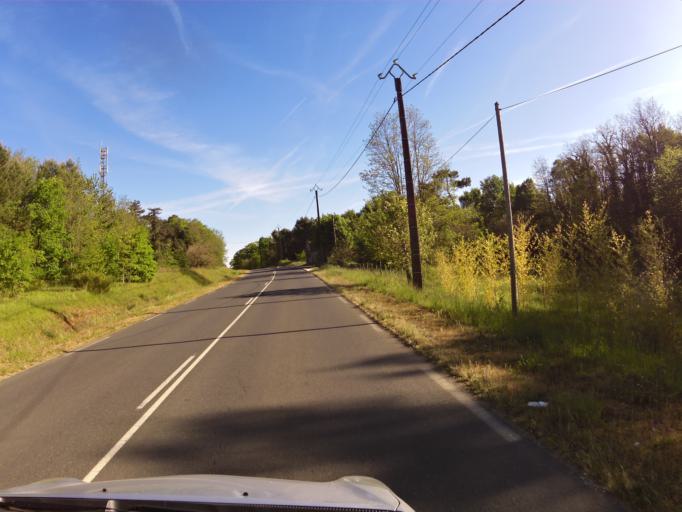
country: FR
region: Aquitaine
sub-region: Departement de la Dordogne
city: Sarlat-la-Caneda
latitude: 44.9900
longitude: 1.2413
